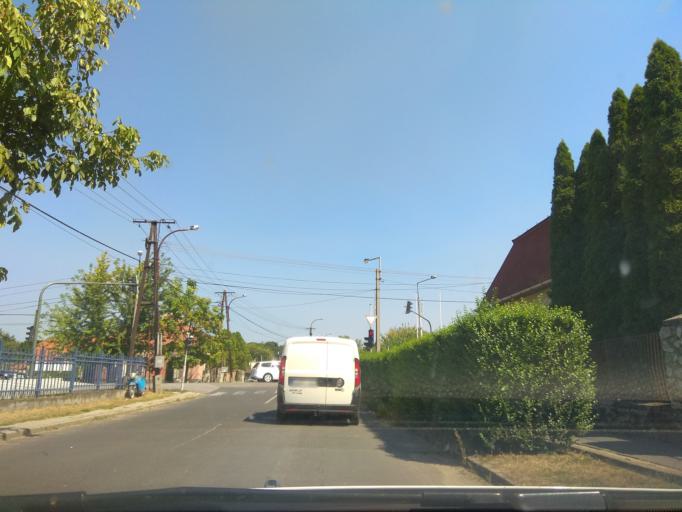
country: HU
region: Borsod-Abauj-Zemplen
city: Miskolc
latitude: 48.0680
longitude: 20.7811
